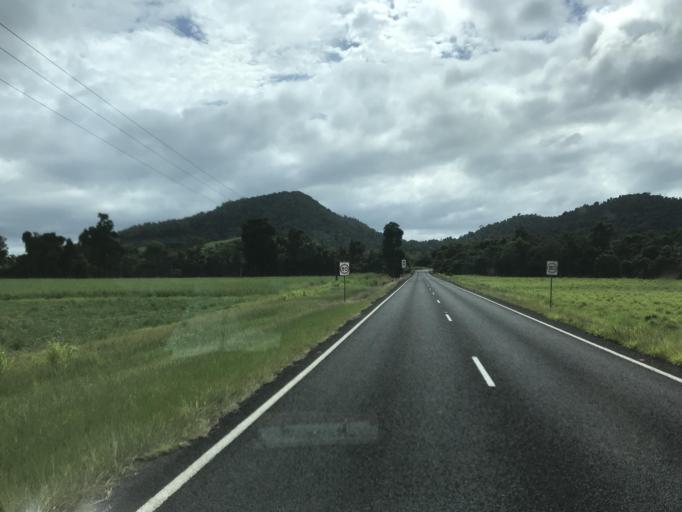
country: AU
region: Queensland
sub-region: Cassowary Coast
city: Innisfail
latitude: -17.8255
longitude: 146.0498
